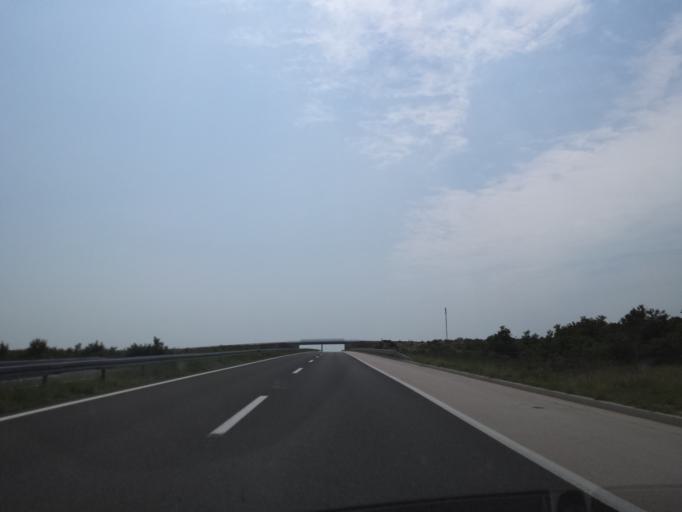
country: HR
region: Zadarska
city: Policnik
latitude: 44.1454
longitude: 15.4206
